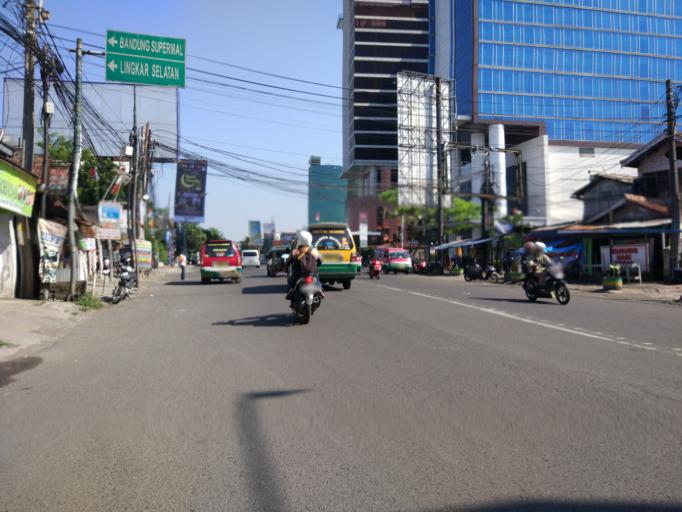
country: ID
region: West Java
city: Bandung
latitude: -6.9282
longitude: 107.6369
